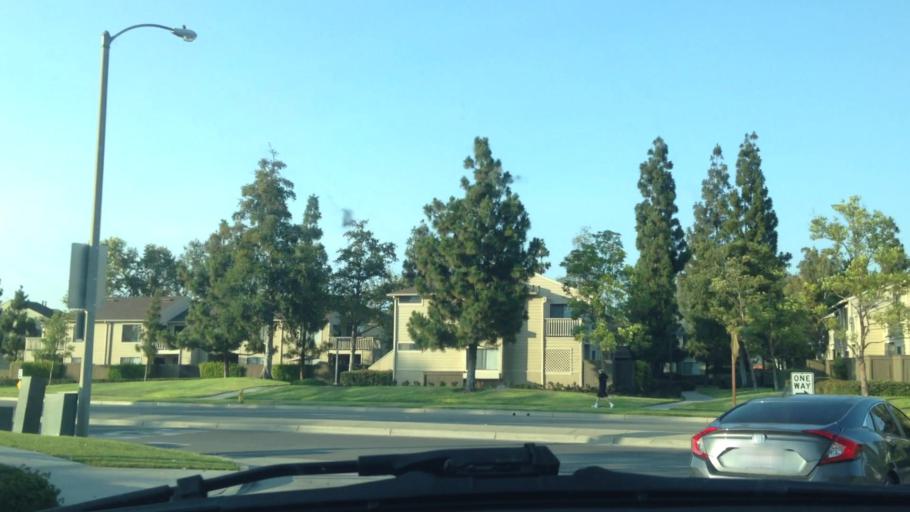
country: US
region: California
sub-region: Orange County
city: Irvine
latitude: 33.6967
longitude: -117.7974
